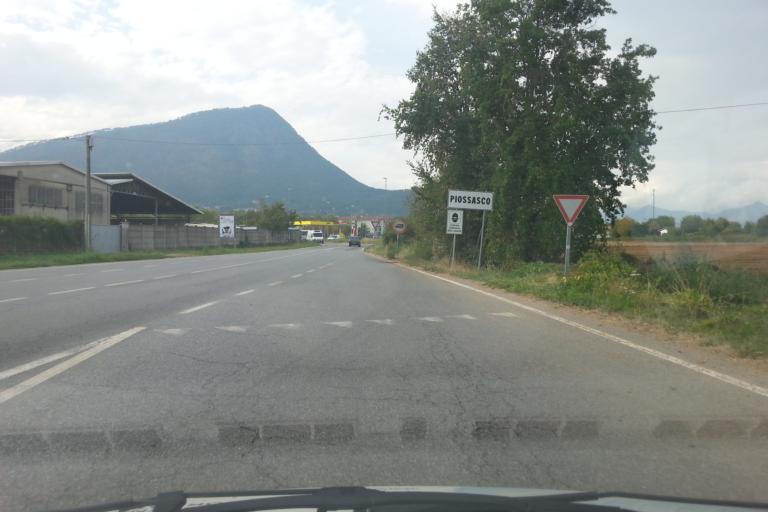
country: IT
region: Piedmont
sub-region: Provincia di Torino
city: Piossasco
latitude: 44.9808
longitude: 7.4724
